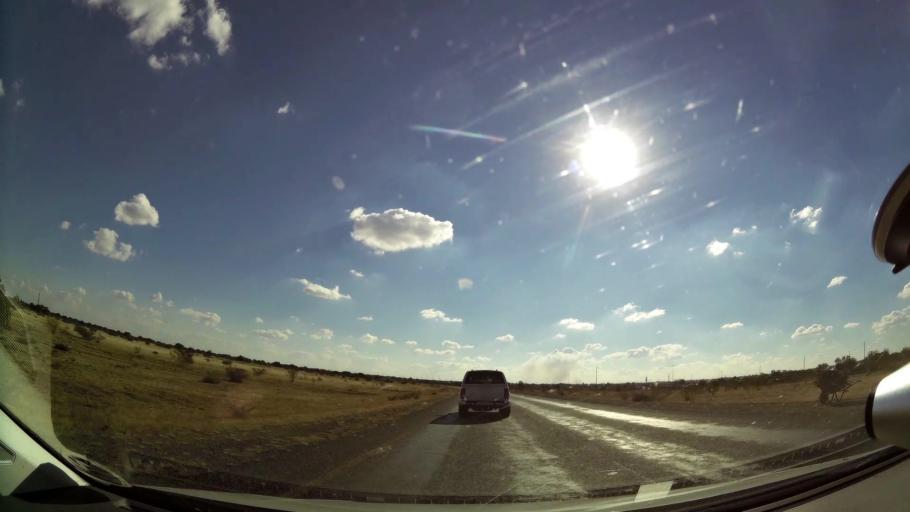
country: ZA
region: Northern Cape
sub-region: Frances Baard District Municipality
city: Kimberley
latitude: -28.7866
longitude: 24.7798
